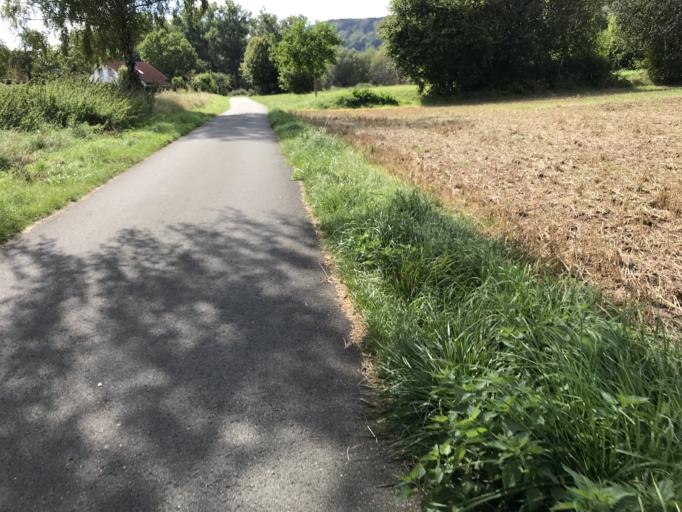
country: DE
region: Hesse
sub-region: Regierungsbezirk Kassel
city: Bad Sooden-Allendorf
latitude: 51.2778
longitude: 9.9672
